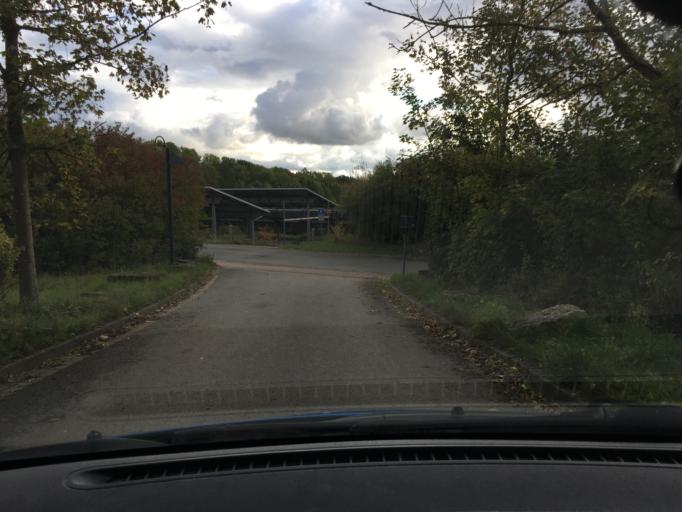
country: DE
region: Lower Saxony
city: Bad Munder am Deister
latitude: 52.2074
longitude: 9.4714
